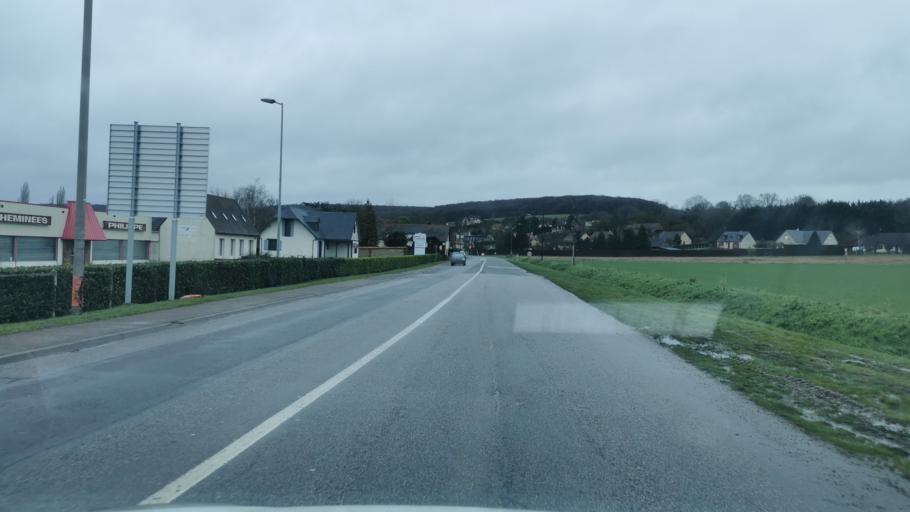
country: FR
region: Haute-Normandie
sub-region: Departement de l'Eure
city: Gravigny
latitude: 49.0621
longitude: 1.1714
